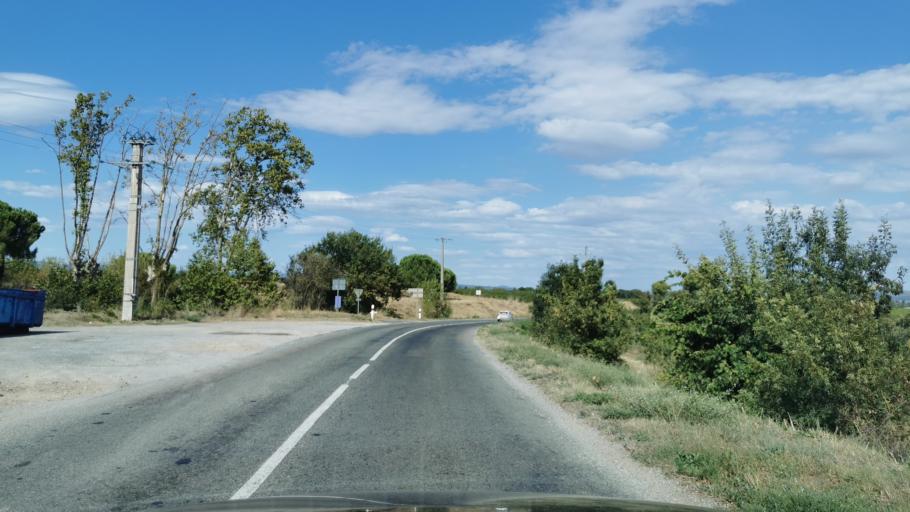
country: FR
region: Languedoc-Roussillon
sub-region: Departement de l'Aude
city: Azille
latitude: 43.2500
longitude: 2.6731
